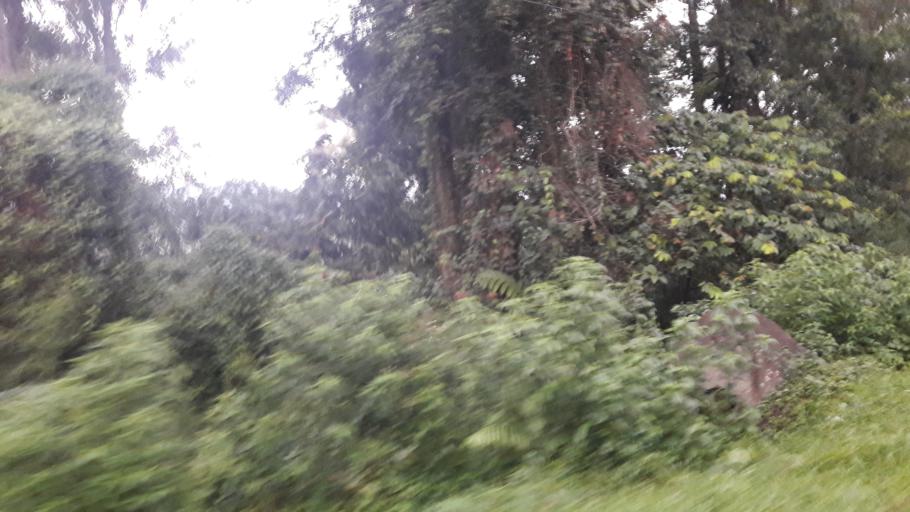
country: ID
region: West Java
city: Cipeundeuy
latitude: -6.6705
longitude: 106.5156
